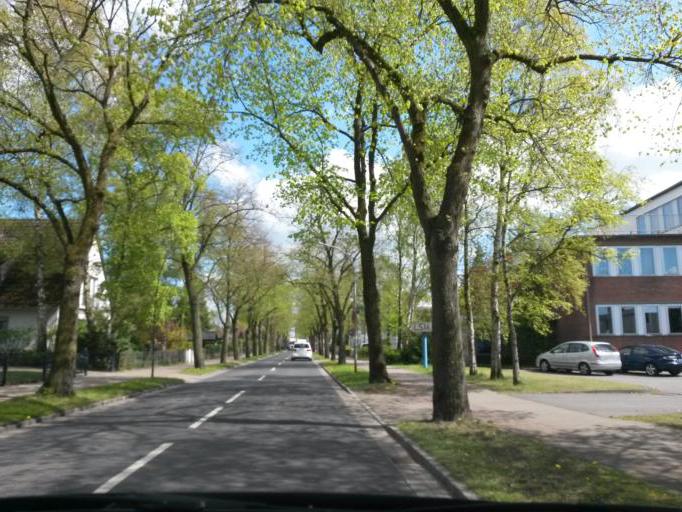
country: DE
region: Schleswig-Holstein
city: Uetersen
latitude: 53.6832
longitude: 9.6788
